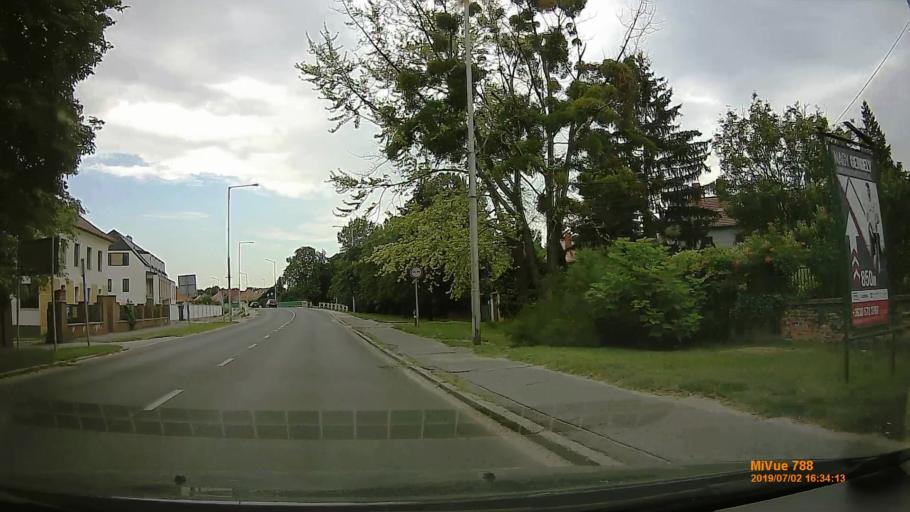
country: HU
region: Gyor-Moson-Sopron
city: Mosonmagyarovar
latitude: 47.8817
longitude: 17.2725
